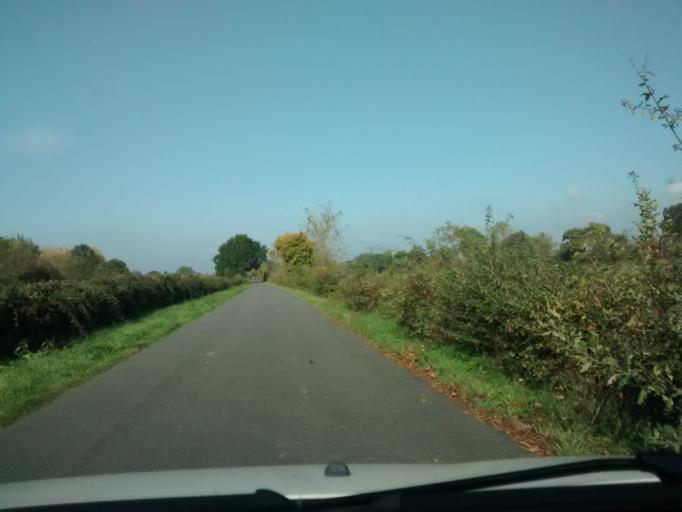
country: FR
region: Pays de la Loire
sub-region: Departement de la Loire-Atlantique
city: Vue
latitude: 47.2428
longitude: -1.8816
